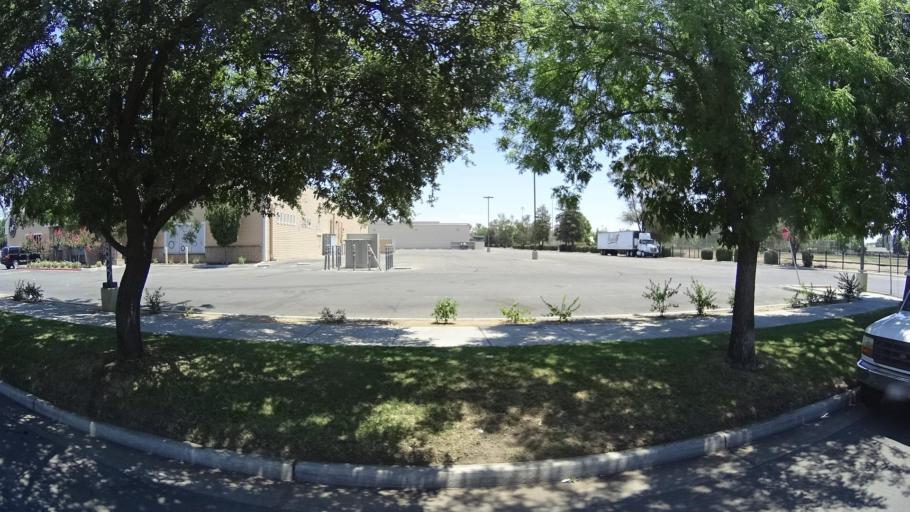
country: US
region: California
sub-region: Fresno County
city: Sunnyside
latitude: 36.7339
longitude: -119.7319
